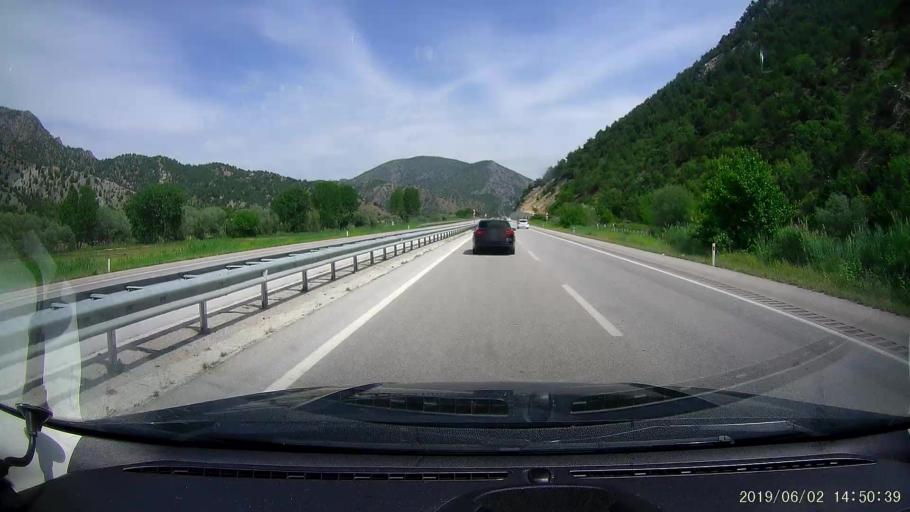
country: TR
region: Corum
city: Kargi
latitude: 41.0702
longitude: 34.5246
